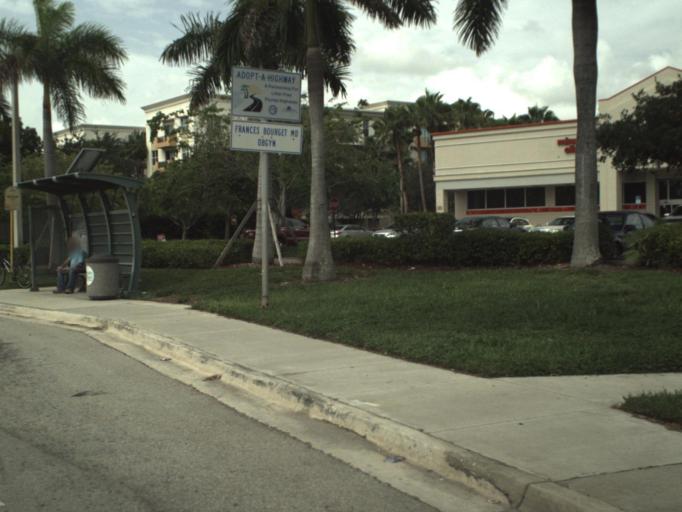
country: US
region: Florida
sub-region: Broward County
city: Terra Mar
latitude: 26.2114
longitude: -80.1070
